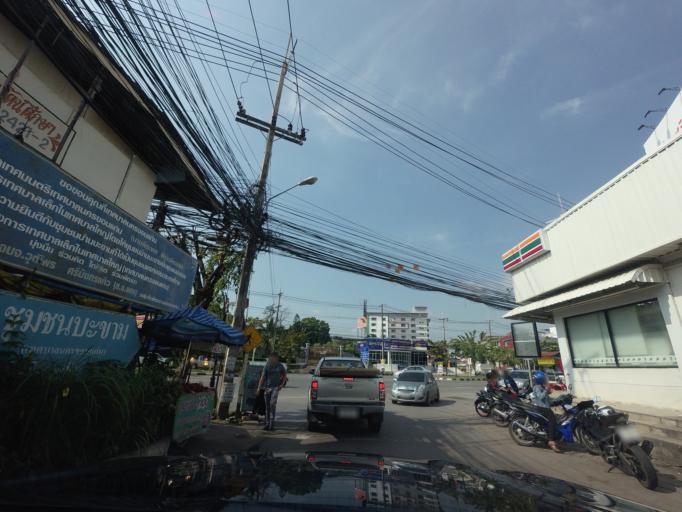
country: TH
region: Khon Kaen
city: Khon Kaen
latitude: 16.4288
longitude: 102.8542
